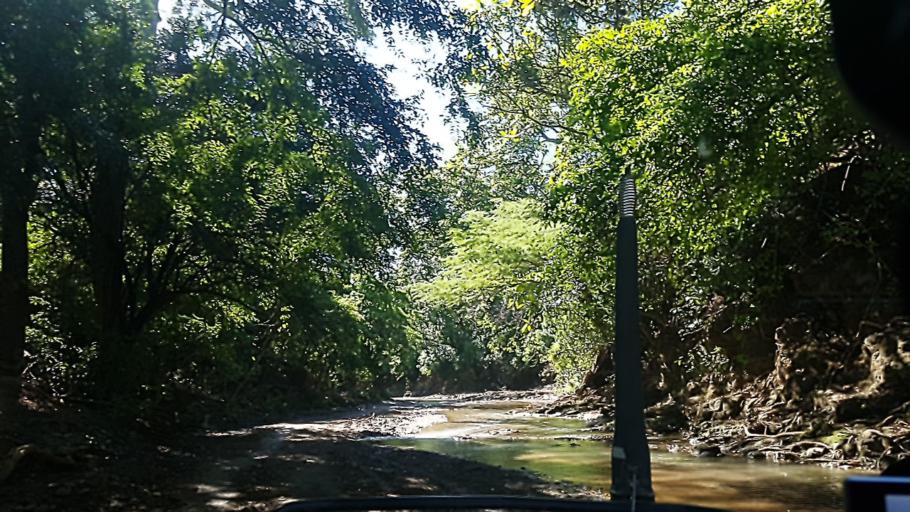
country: NI
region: Rivas
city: Tola
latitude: 11.5415
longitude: -86.1089
